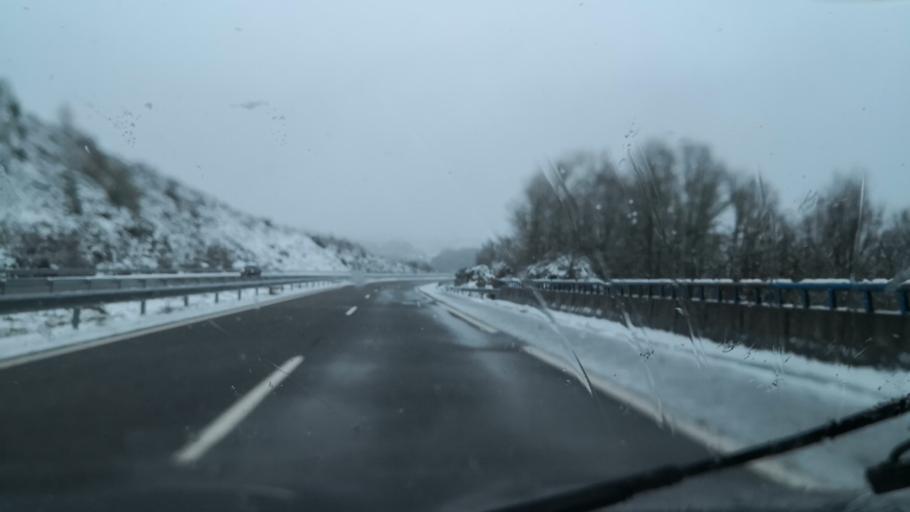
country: ES
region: Galicia
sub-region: Provincia de Ourense
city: Rios
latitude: 41.9896
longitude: -7.2435
